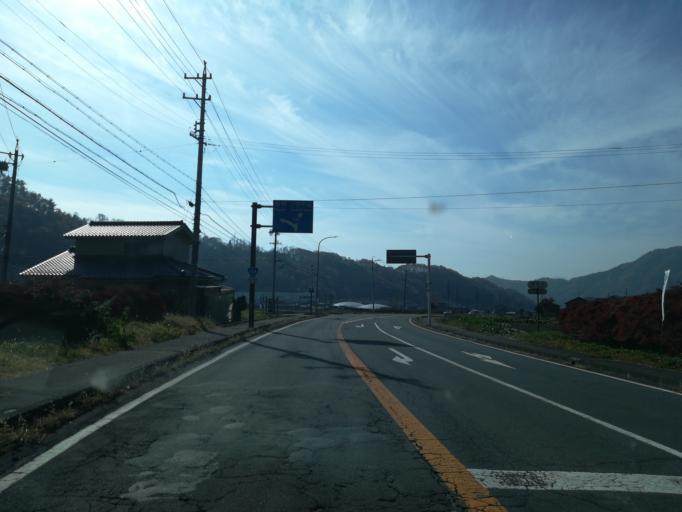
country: JP
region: Nagano
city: Ueda
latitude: 36.4467
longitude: 138.3203
